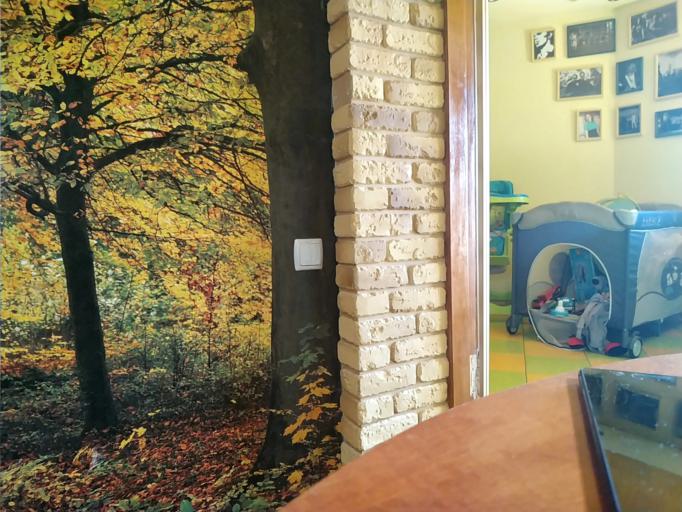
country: RU
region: Tverskaya
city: Krasnomayskiy
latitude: 57.6190
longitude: 34.4141
